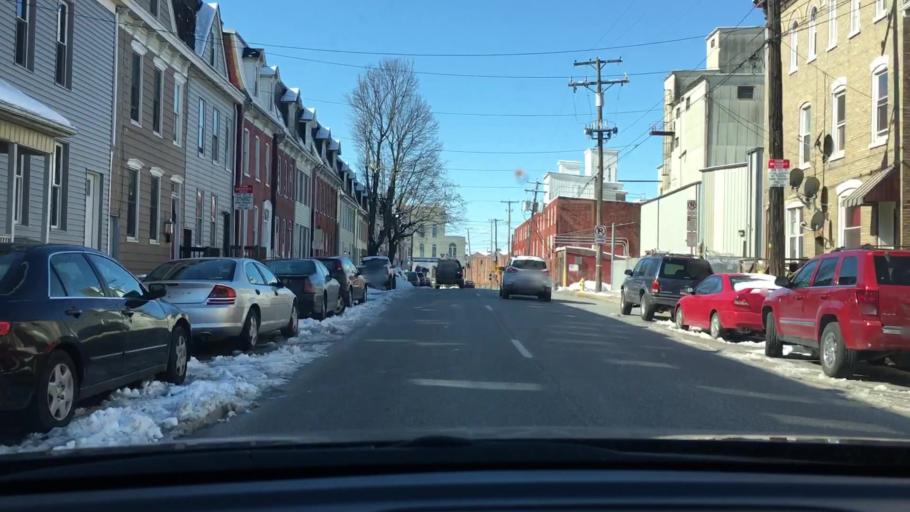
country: US
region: Pennsylvania
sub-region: York County
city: West York
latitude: 39.9582
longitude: -76.7466
